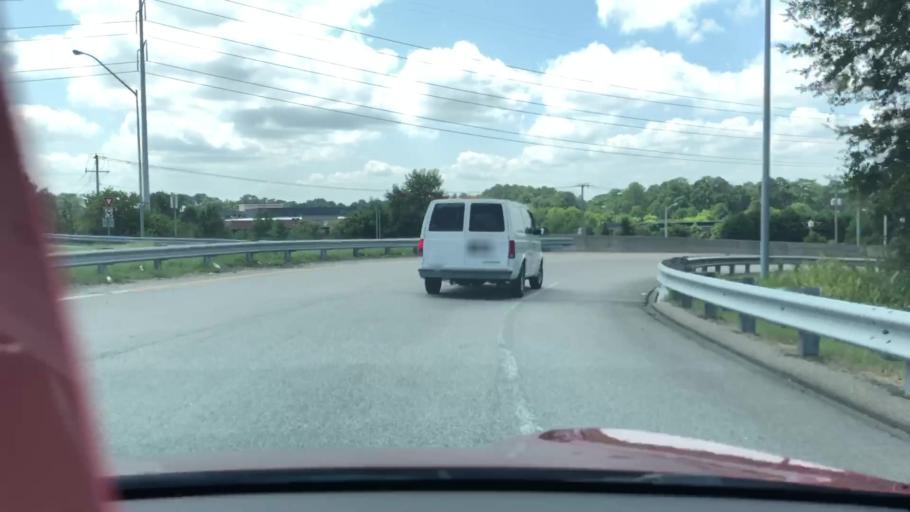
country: US
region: Virginia
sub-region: City of Chesapeake
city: Chesapeake
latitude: 36.8424
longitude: -76.2104
